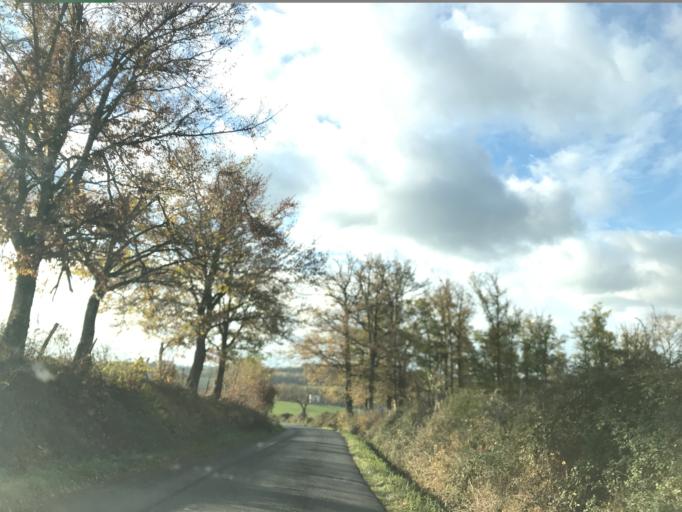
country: FR
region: Auvergne
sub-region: Departement du Puy-de-Dome
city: Courpiere
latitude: 45.7559
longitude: 3.6038
